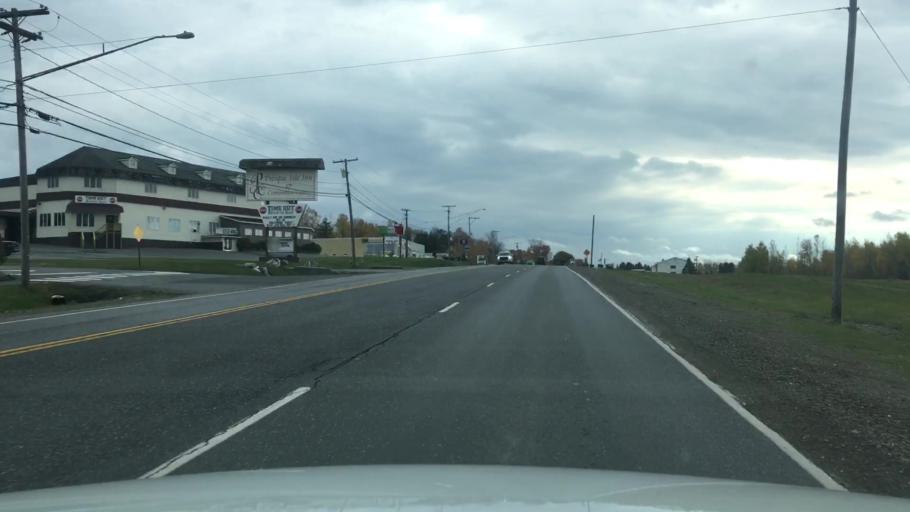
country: US
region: Maine
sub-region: Aroostook County
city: Presque Isle
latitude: 46.6682
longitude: -68.0124
